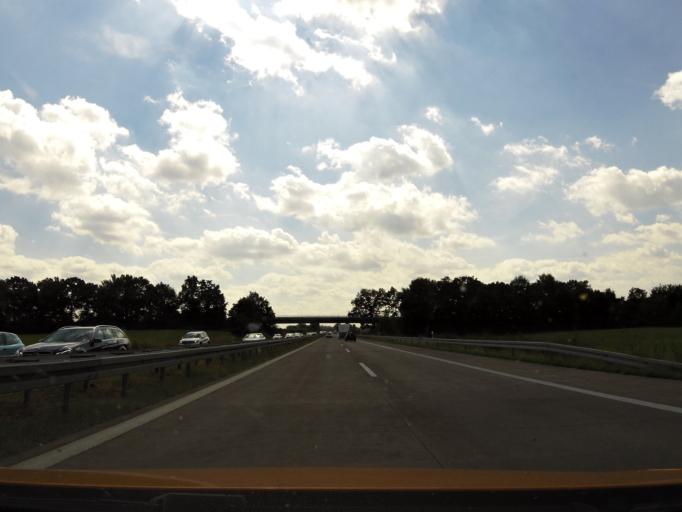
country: DE
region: Brandenburg
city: Althuttendorf
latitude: 52.9723
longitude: 13.8165
